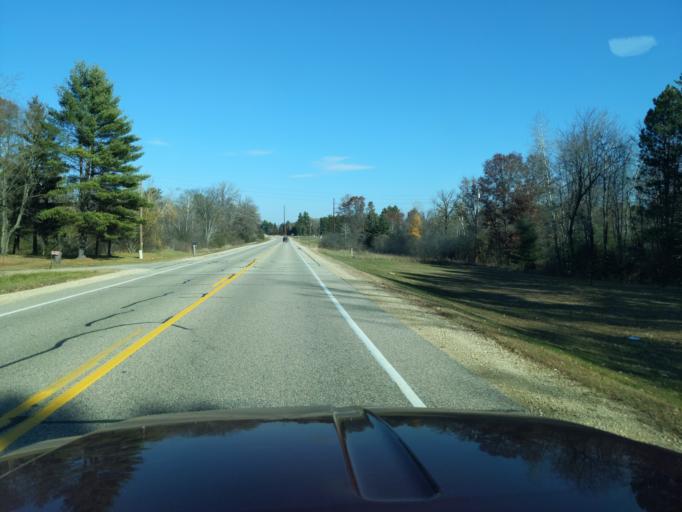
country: US
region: Wisconsin
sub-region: Waushara County
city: Wautoma
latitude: 44.0512
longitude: -89.2940
